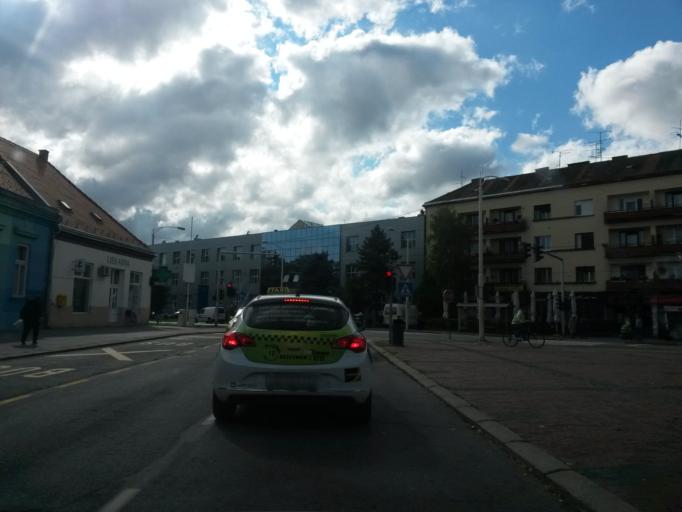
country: HR
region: Osjecko-Baranjska
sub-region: Grad Osijek
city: Osijek
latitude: 45.5553
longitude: 18.7202
